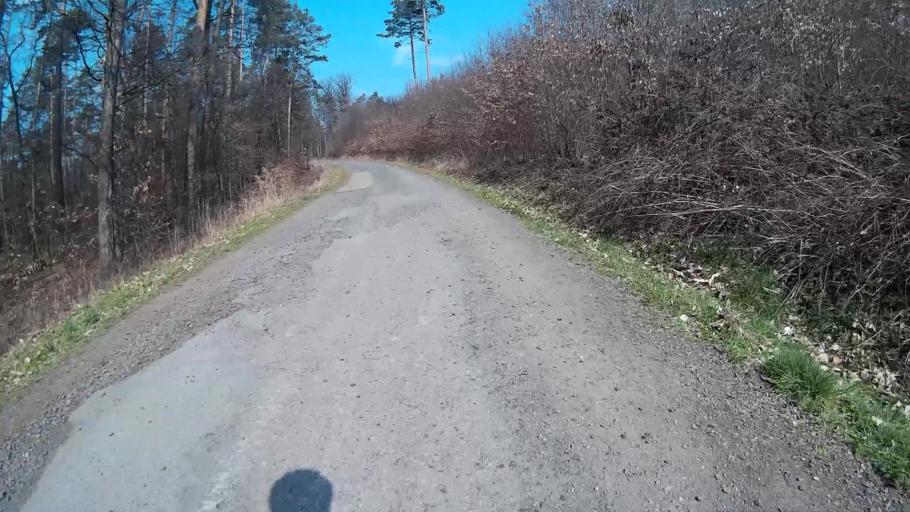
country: CZ
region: South Moravian
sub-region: Mesto Brno
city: Mokra Hora
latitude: 49.2571
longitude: 16.6083
